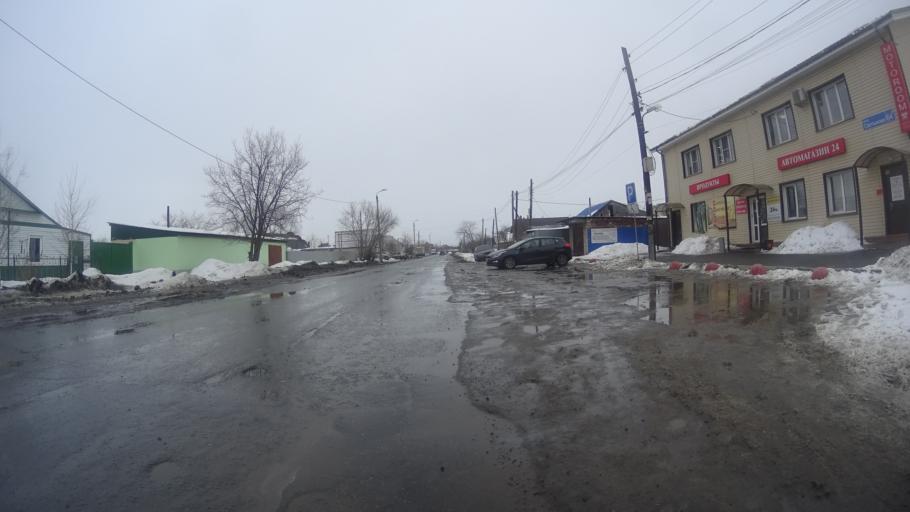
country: RU
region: Chelyabinsk
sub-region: Gorod Chelyabinsk
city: Chelyabinsk
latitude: 55.1298
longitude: 61.3897
